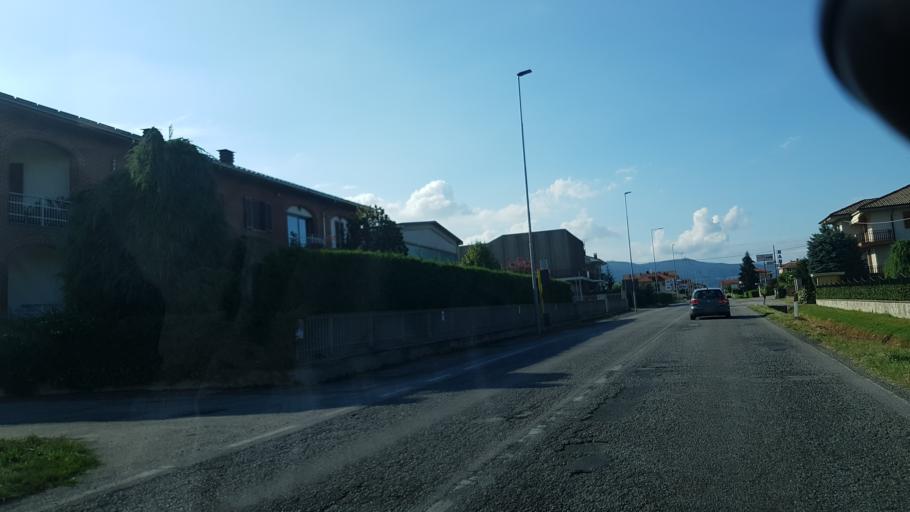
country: IT
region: Piedmont
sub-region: Provincia di Cuneo
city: Roata Rossi
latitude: 44.4730
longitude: 7.5102
